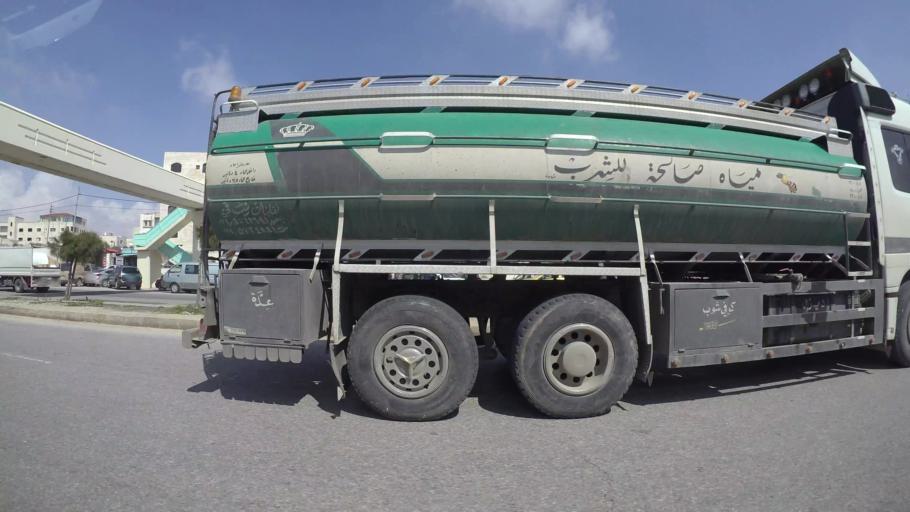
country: JO
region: Amman
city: Al Bunayyat ash Shamaliyah
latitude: 31.9010
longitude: 35.8937
